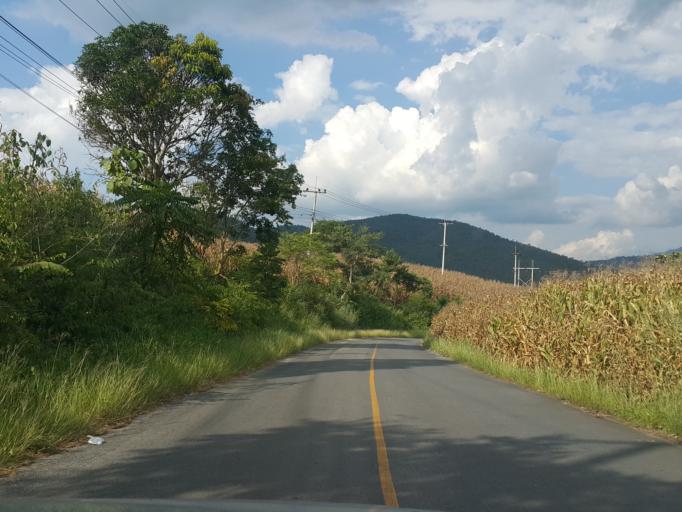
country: TH
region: Chiang Mai
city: Mae Chaem
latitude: 18.5319
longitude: 98.3688
